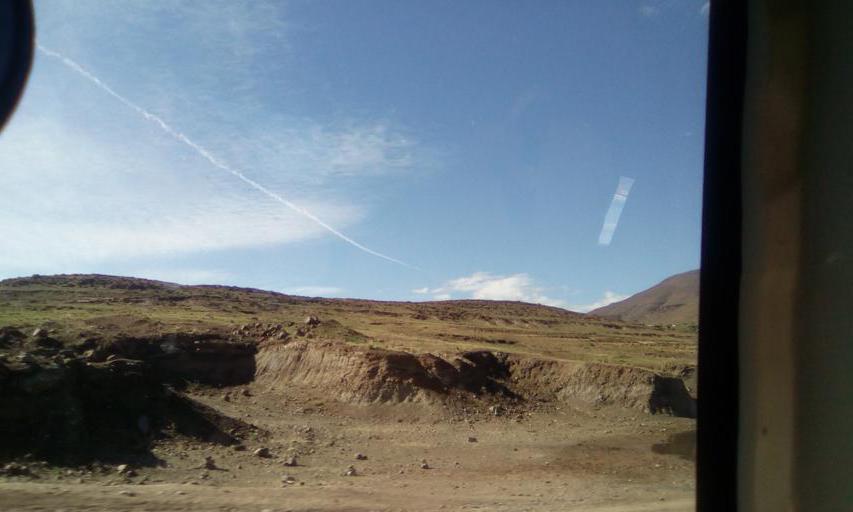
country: LS
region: Qacha's Nek
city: Qacha's Nek
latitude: -30.0406
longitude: 28.2449
